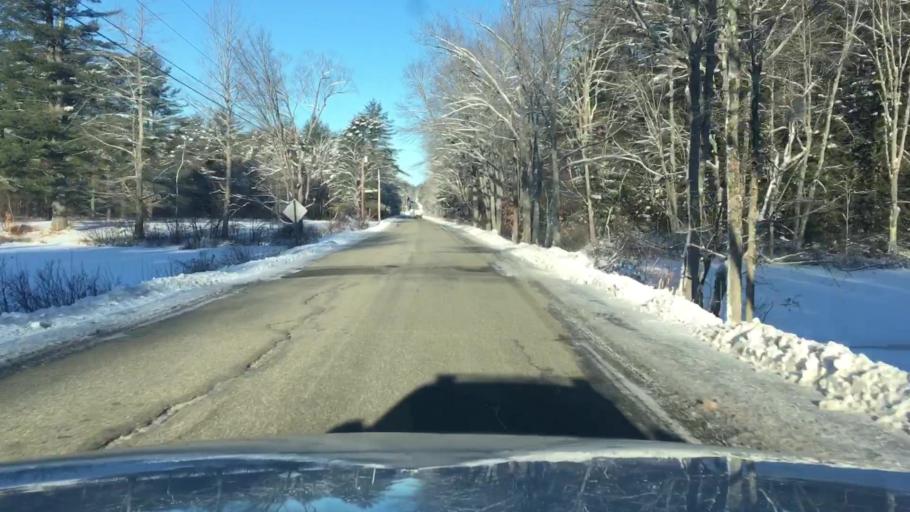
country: US
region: Maine
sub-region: Kennebec County
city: Belgrade
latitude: 44.4104
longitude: -69.8665
